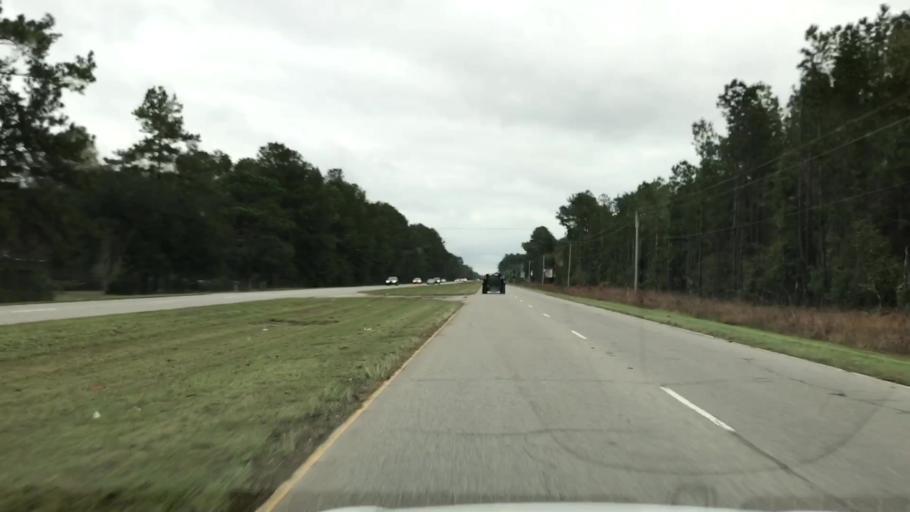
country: US
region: South Carolina
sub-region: Georgetown County
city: Georgetown
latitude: 33.3053
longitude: -79.3365
